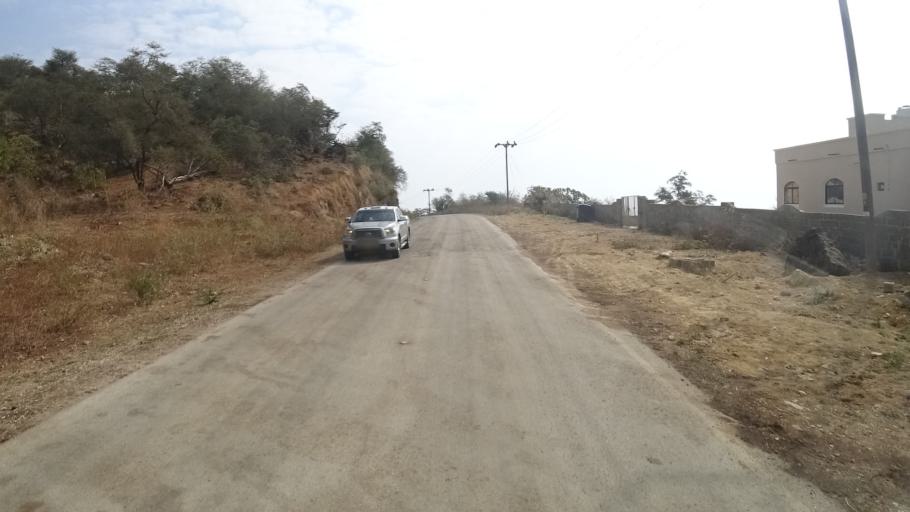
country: YE
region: Al Mahrah
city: Hawf
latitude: 16.7072
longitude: 53.2175
